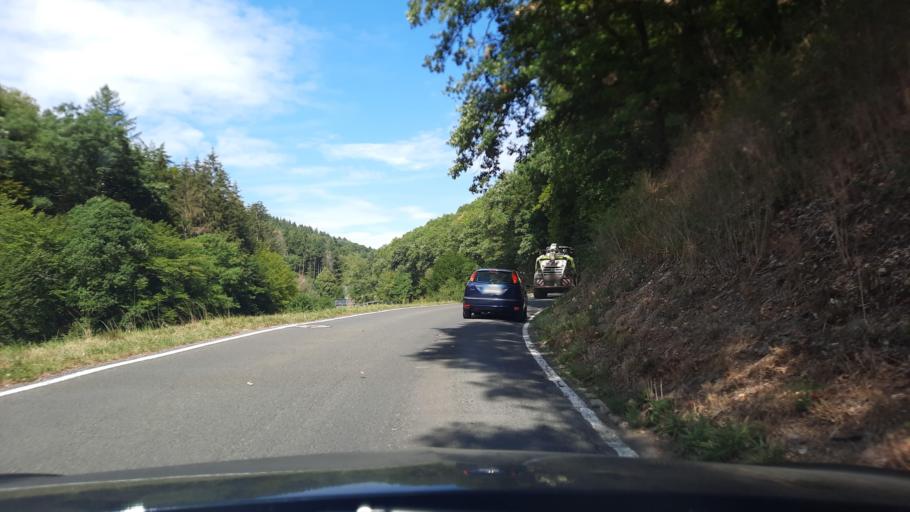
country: DE
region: Rheinland-Pfalz
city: Saarburg
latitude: 49.6143
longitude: 6.5349
